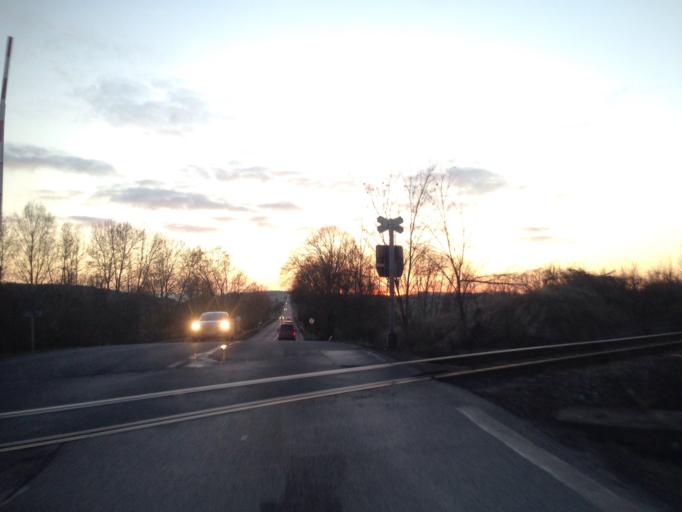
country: CZ
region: Central Bohemia
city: Rakovnik
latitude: 50.1711
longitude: 13.7158
